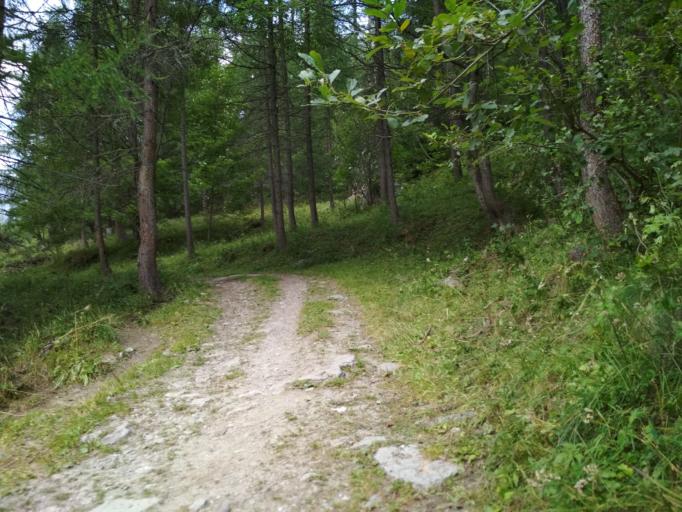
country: IT
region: Aosta Valley
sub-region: Valle d'Aosta
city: Gressoney-La-Trinite
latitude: 45.8145
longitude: 7.8279
